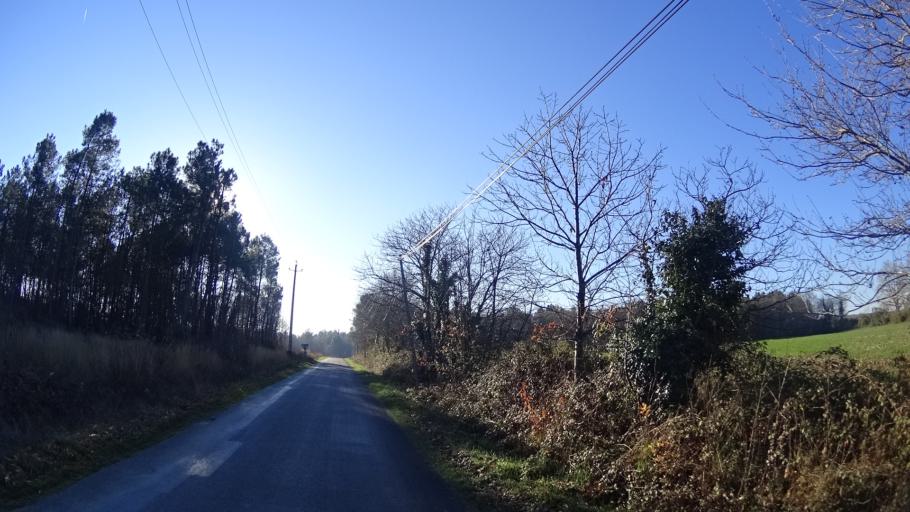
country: FR
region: Brittany
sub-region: Departement du Morbihan
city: Allaire
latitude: 47.6111
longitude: -2.1766
